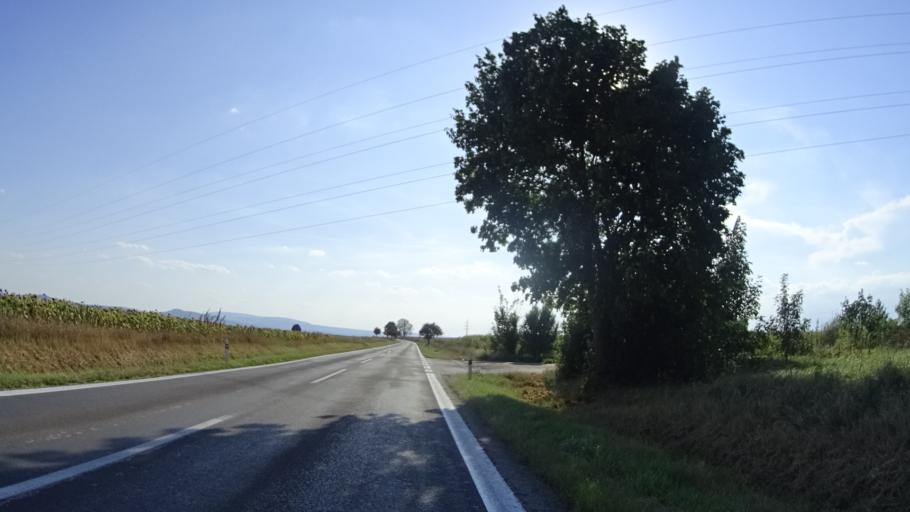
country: HU
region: Komarom-Esztergom
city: Tat
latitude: 47.7936
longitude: 18.6580
